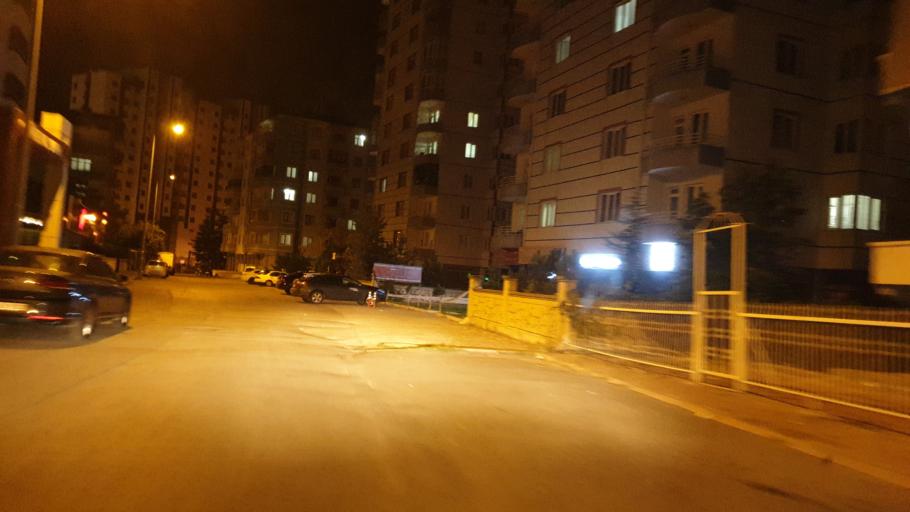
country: TR
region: Kayseri
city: Talas
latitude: 38.6957
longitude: 35.5430
